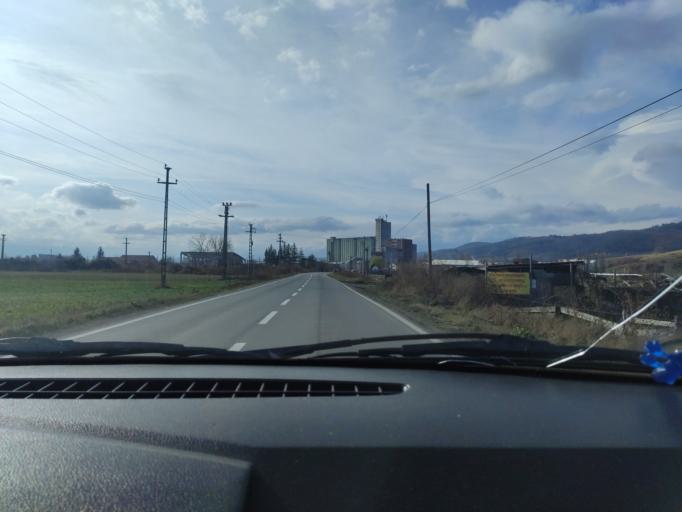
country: RO
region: Brasov
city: Codlea
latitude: 45.7116
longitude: 25.4639
